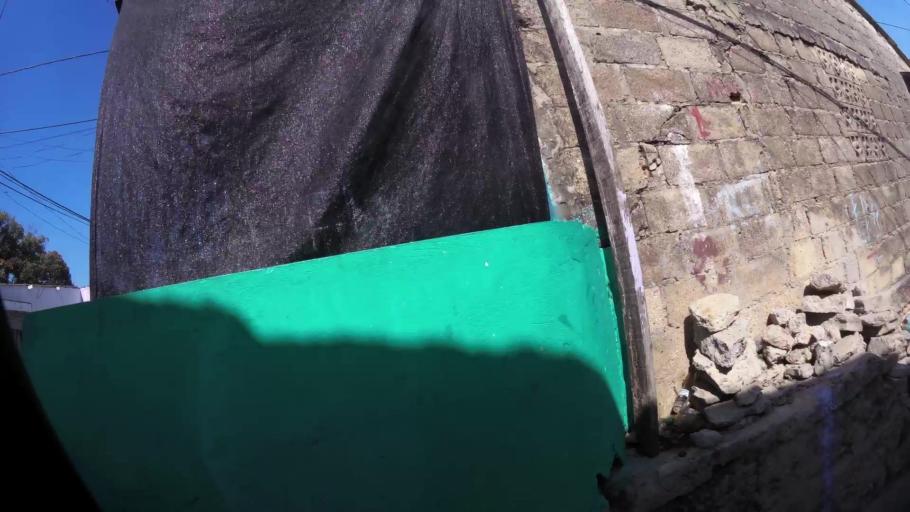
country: CO
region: Bolivar
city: Cartagena
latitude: 10.3962
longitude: -75.5013
